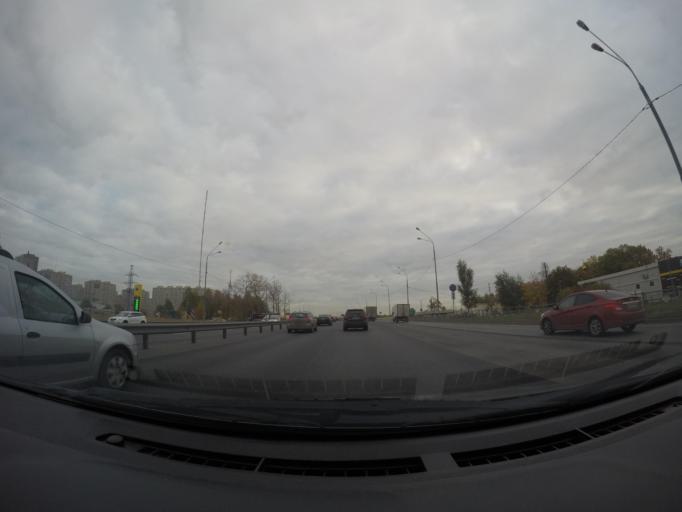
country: RU
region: Moscow
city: Vostochnyy
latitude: 55.7862
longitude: 37.8825
